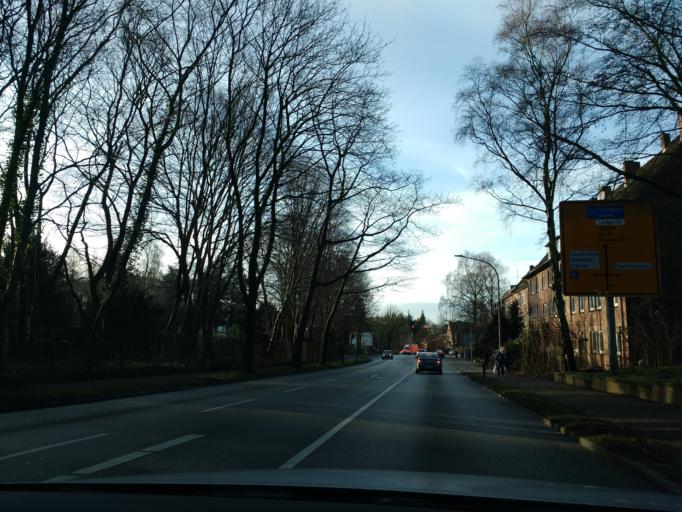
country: DE
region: Schleswig-Holstein
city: Itzehoe
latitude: 53.9313
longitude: 9.5197
